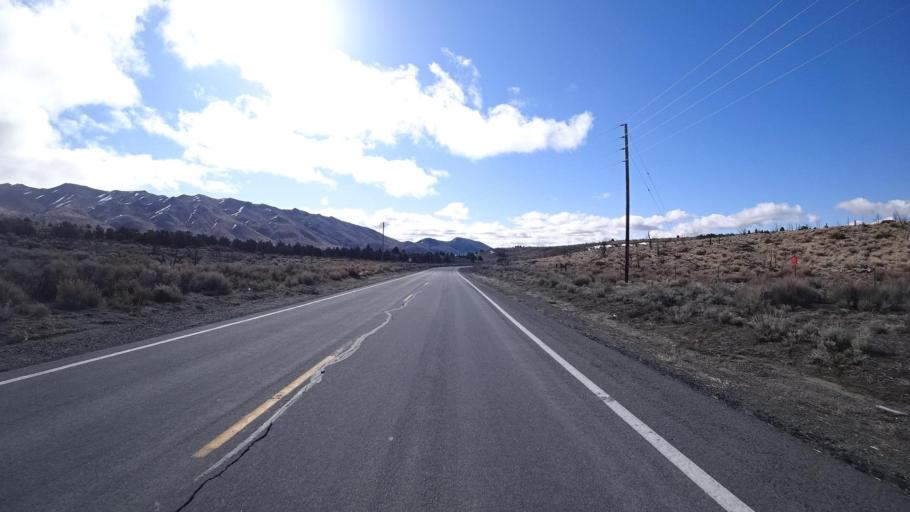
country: US
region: Nevada
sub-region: Washoe County
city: Cold Springs
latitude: 39.7765
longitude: -119.8938
